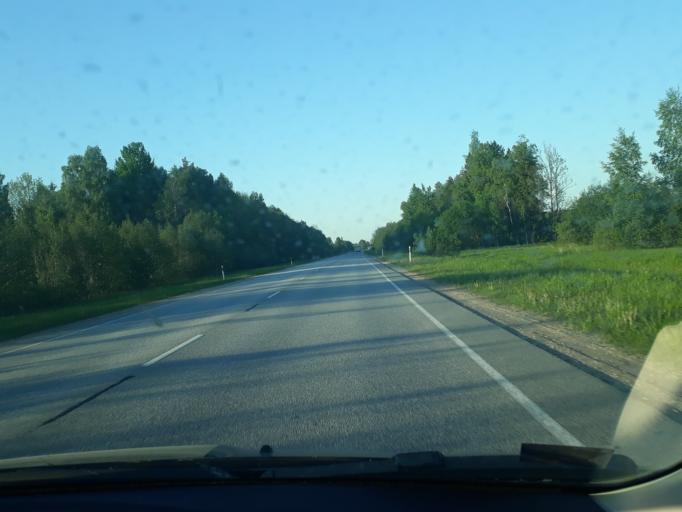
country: EE
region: Paernumaa
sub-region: Sindi linn
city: Sindi
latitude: 58.4693
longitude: 24.7113
